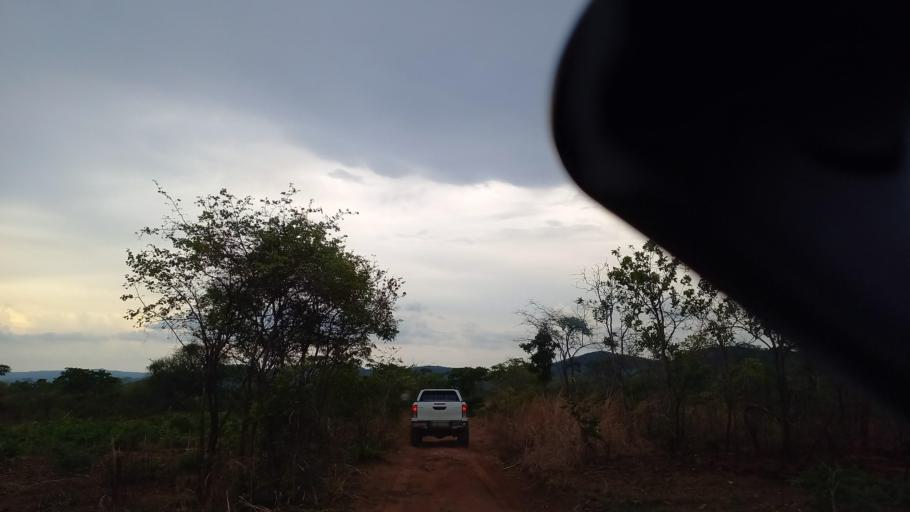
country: ZM
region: Lusaka
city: Kafue
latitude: -16.0495
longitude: 28.3333
